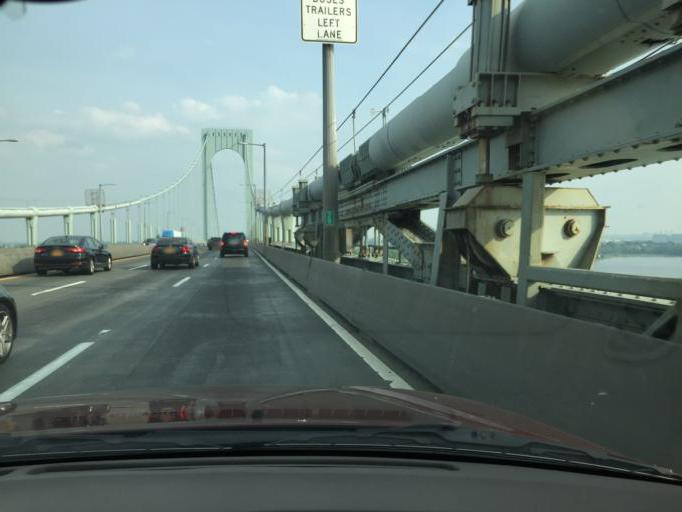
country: US
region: New York
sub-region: Bronx
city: The Bronx
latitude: 40.8021
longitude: -73.8300
